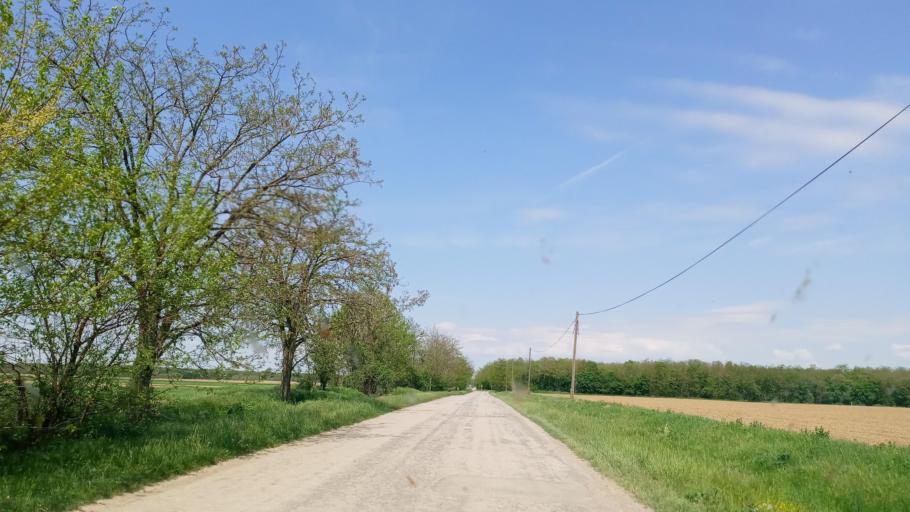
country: HU
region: Baranya
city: Boly
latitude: 45.8793
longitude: 18.5751
